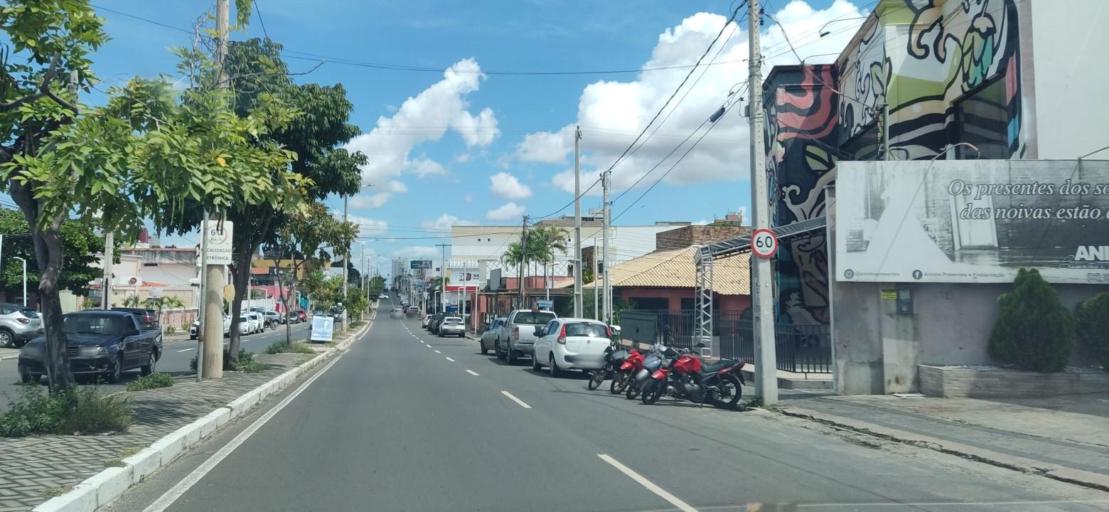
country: BR
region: Piaui
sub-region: Teresina
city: Teresina
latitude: -5.0640
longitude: -42.7941
